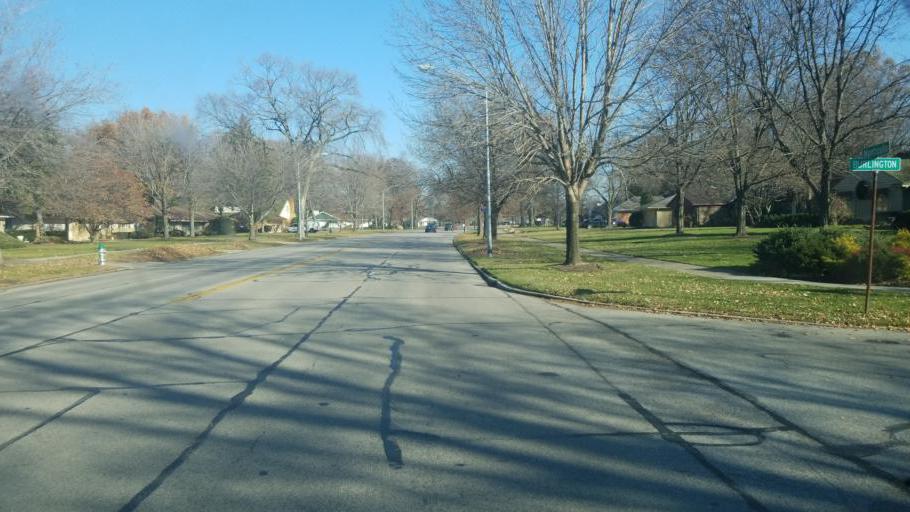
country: US
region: Ohio
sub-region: Cuyahoga County
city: Cleveland Heights
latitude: 41.5215
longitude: -81.5671
